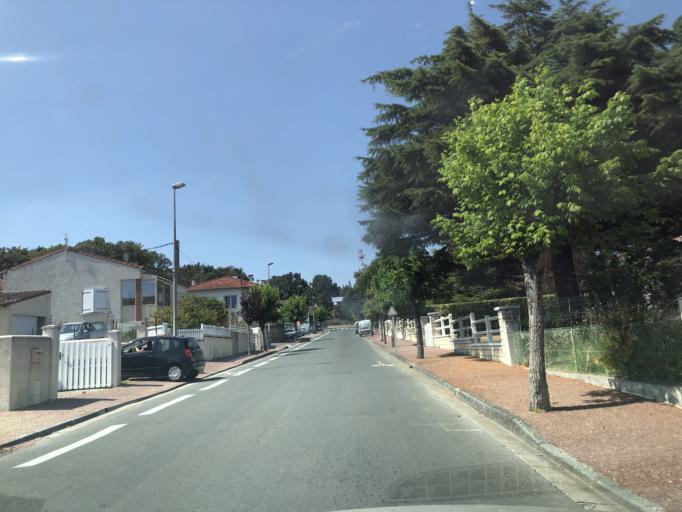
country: FR
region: Poitou-Charentes
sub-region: Departement de la Charente-Maritime
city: Meschers-sur-Gironde
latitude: 45.5642
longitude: -0.9604
